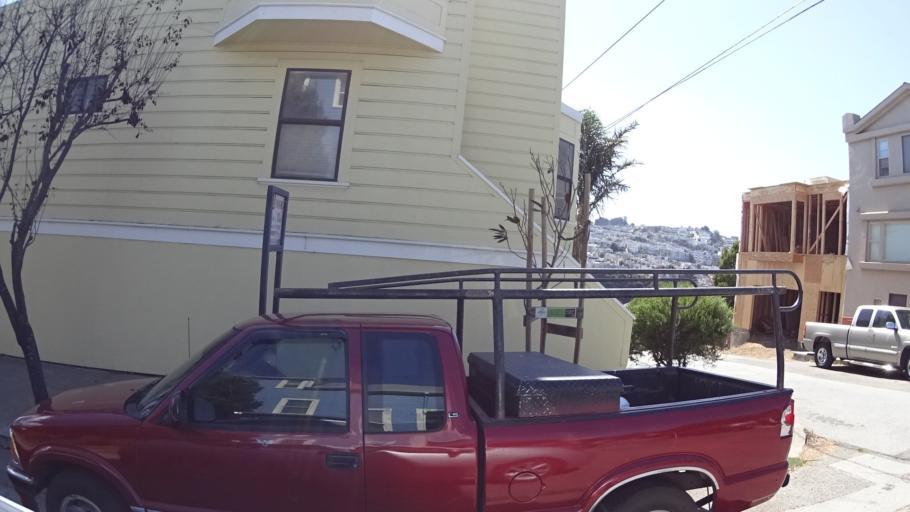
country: US
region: California
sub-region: San Francisco County
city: San Francisco
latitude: 37.7339
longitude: -122.4174
